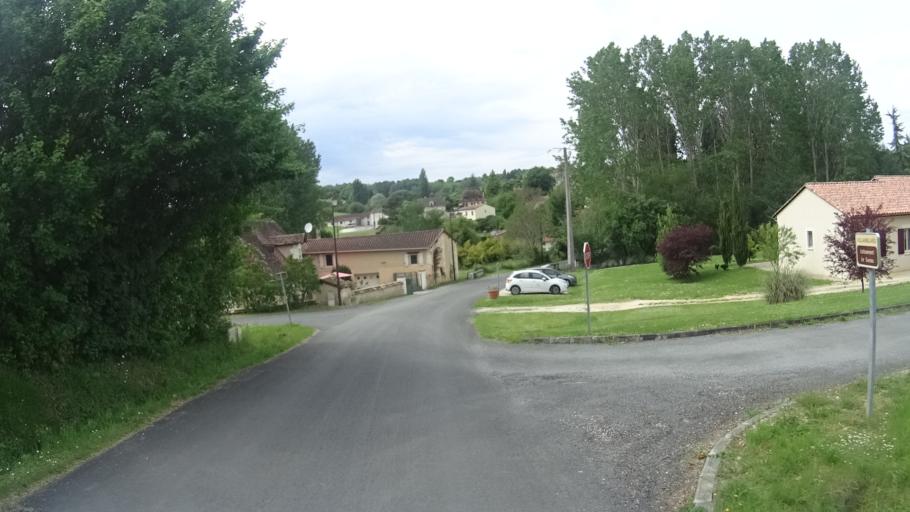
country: FR
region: Aquitaine
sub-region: Departement de la Dordogne
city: Neuvic
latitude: 45.0182
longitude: 0.5390
